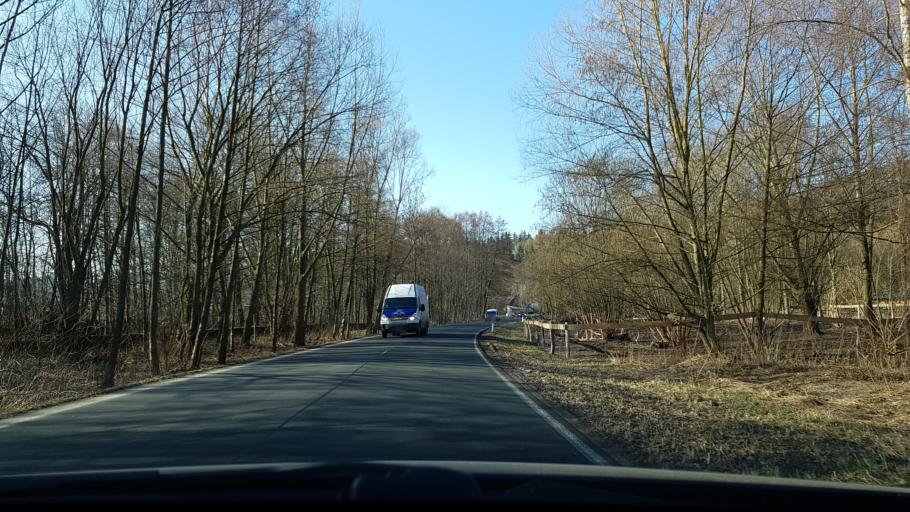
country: CZ
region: Olomoucky
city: Dolni Bohdikov
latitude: 50.0296
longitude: 16.9023
